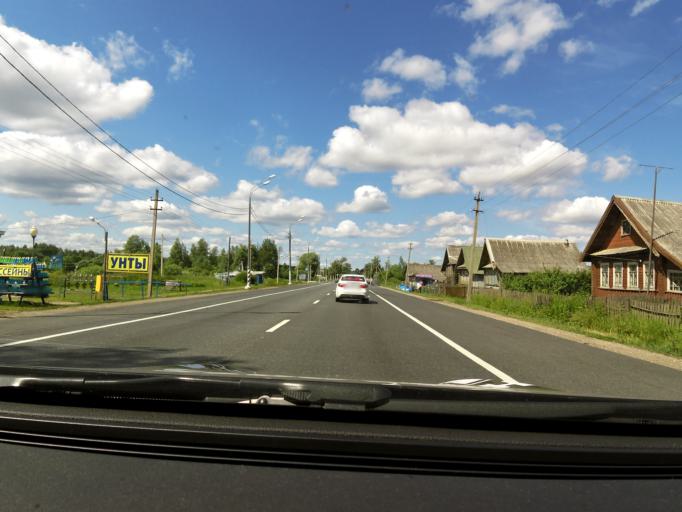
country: RU
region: Tverskaya
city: Kuzhenkino
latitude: 57.7264
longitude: 34.0697
